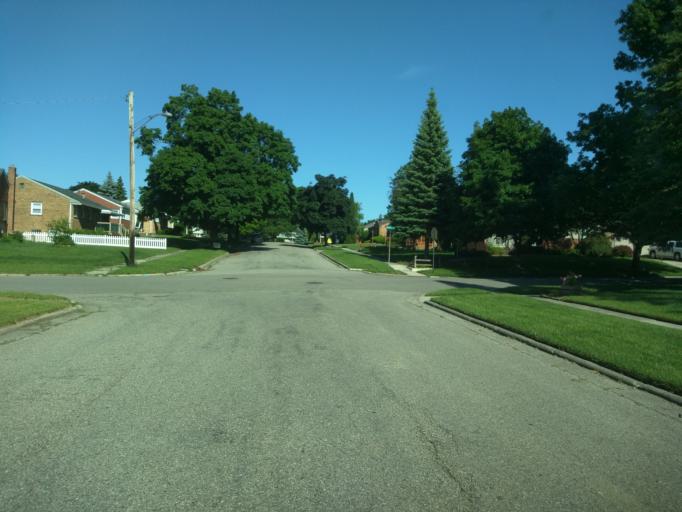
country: US
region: Michigan
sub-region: Ingham County
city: Edgemont Park
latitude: 42.7459
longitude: -84.5983
